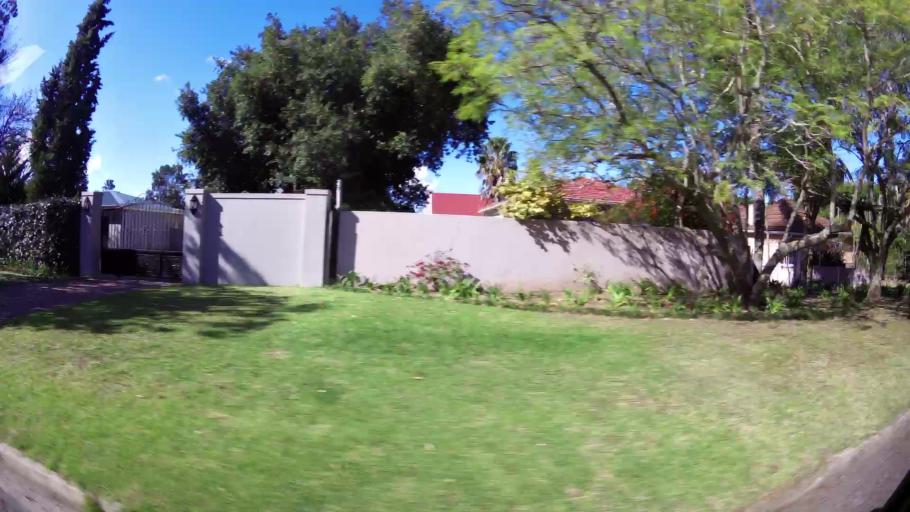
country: ZA
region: Western Cape
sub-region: Eden District Municipality
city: George
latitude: -33.9461
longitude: 22.4661
